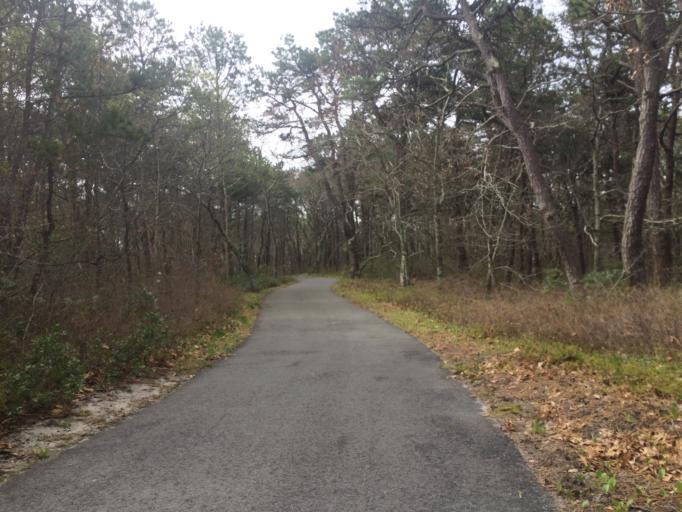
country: US
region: Massachusetts
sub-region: Barnstable County
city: Provincetown
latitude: 42.0587
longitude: -70.2008
